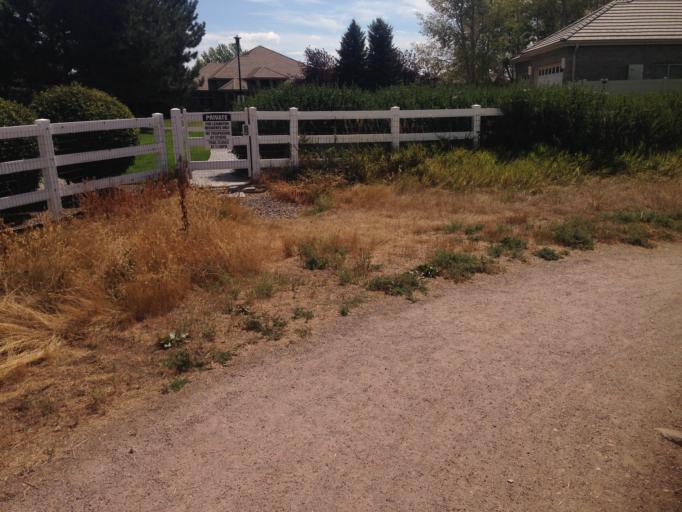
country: US
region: Colorado
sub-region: Adams County
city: Northglenn
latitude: 39.9539
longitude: -105.0072
